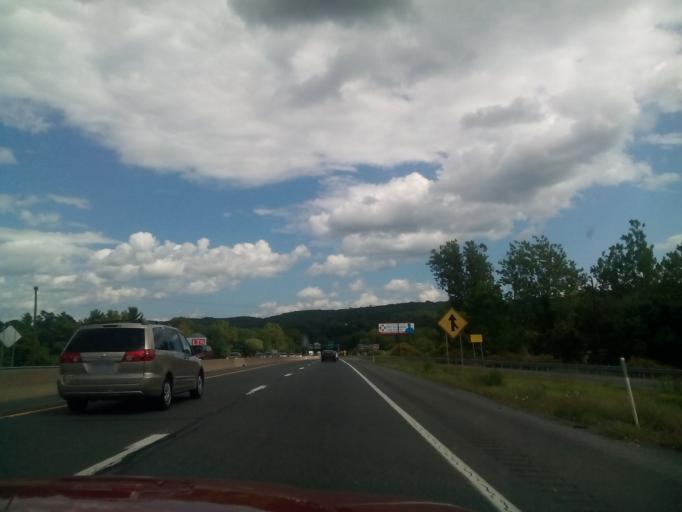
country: US
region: Pennsylvania
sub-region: Monroe County
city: Stroudsburg
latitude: 40.9802
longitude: -75.2062
